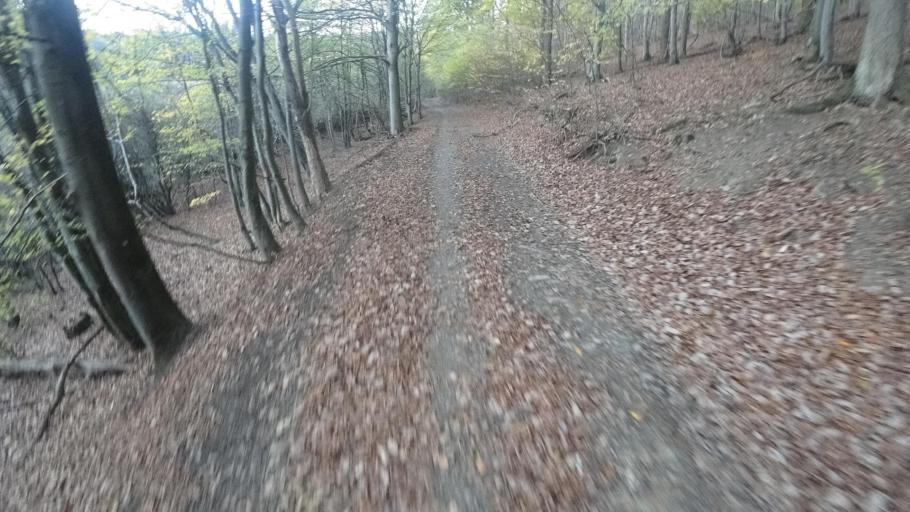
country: DE
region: Rheinland-Pfalz
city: Berg
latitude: 50.5336
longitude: 6.9560
